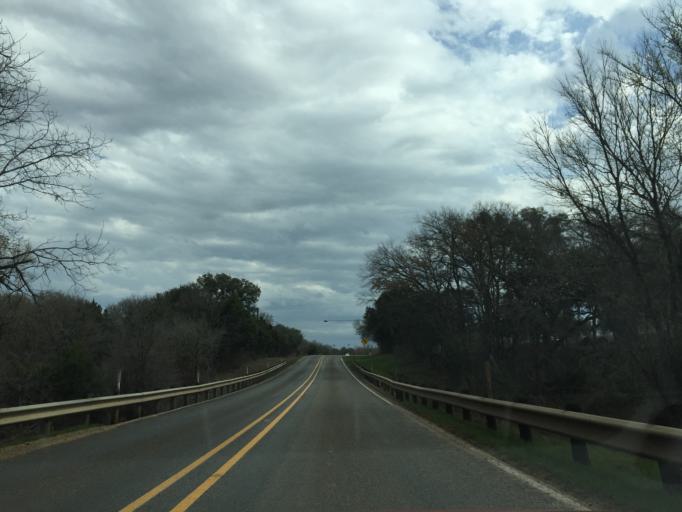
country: US
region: Texas
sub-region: Williamson County
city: Leander
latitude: 30.6603
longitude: -97.9432
